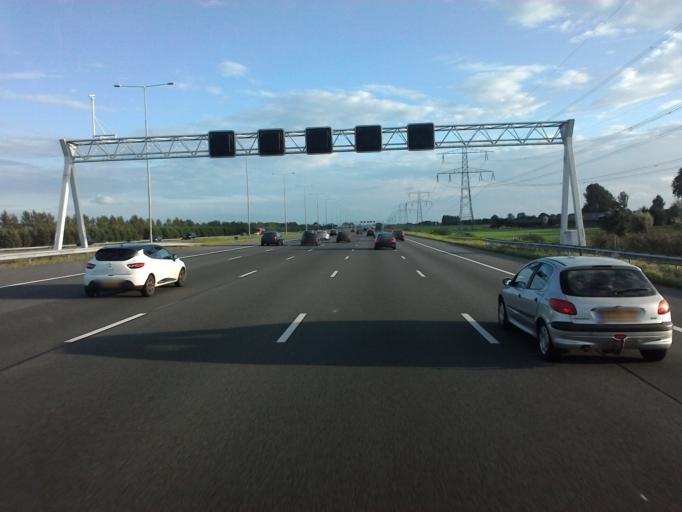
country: NL
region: Utrecht
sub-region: Stichtse Vecht
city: Breukelen
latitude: 52.2018
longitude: 4.9862
